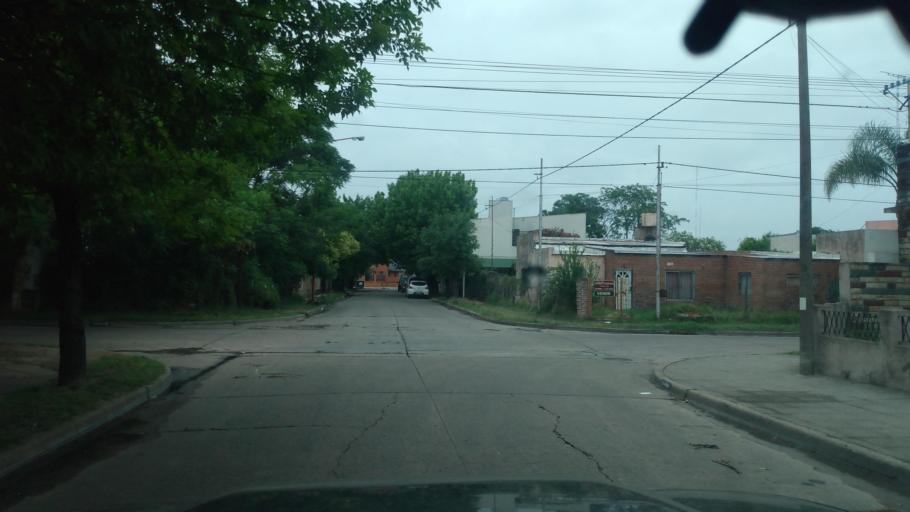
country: AR
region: Buenos Aires
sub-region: Partido de Lujan
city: Lujan
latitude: -34.5738
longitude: -59.1174
